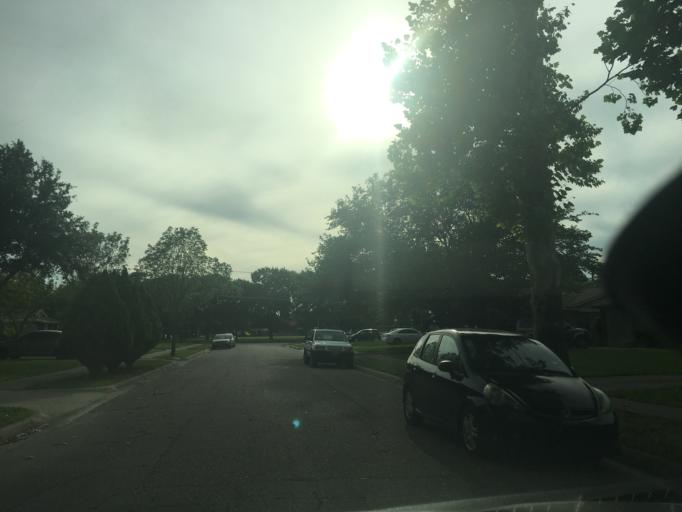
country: US
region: Texas
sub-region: Dallas County
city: Richardson
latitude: 32.9511
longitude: -96.7171
